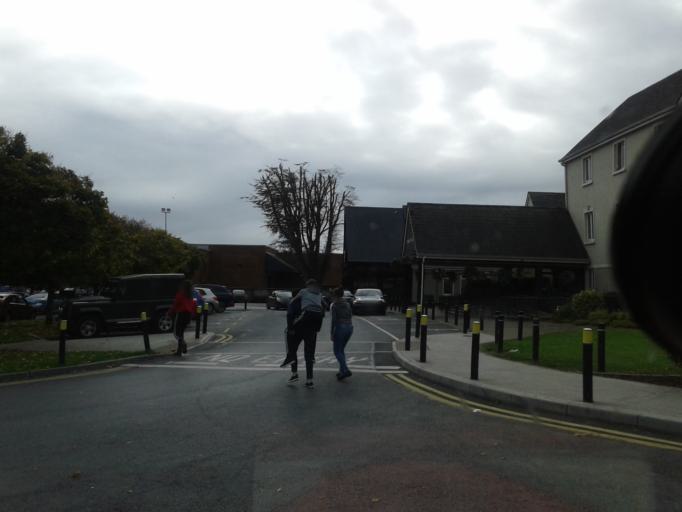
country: IE
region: Munster
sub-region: An Clar
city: Ennis
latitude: 52.8441
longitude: -8.9811
